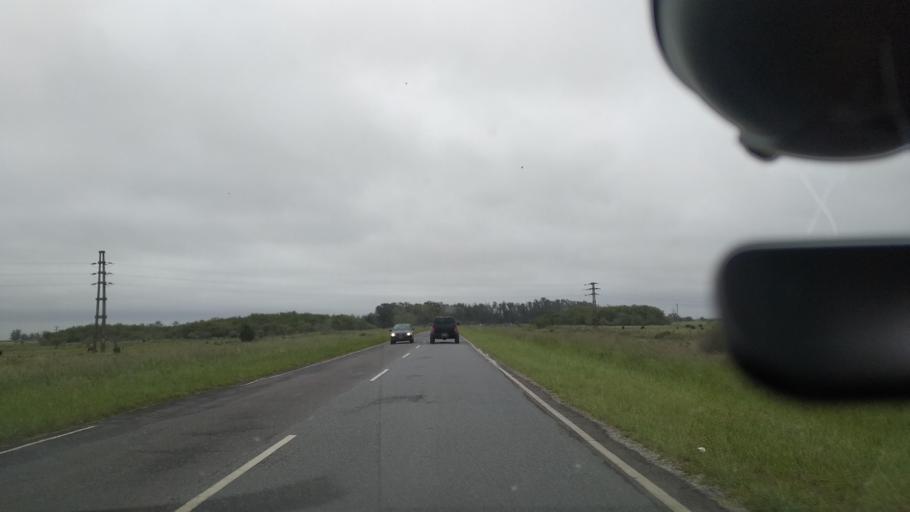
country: AR
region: Buenos Aires
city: Veronica
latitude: -35.5177
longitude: -57.3322
